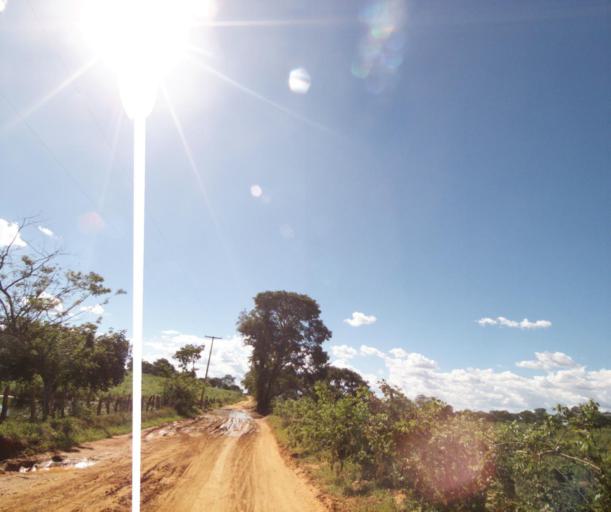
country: BR
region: Bahia
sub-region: Carinhanha
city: Carinhanha
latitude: -14.1825
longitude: -44.5063
